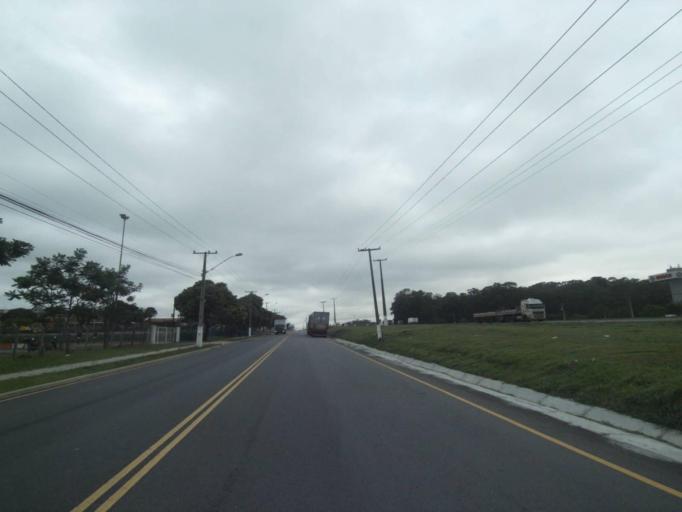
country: BR
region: Parana
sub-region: Araucaria
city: Araucaria
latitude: -25.5311
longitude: -49.3231
